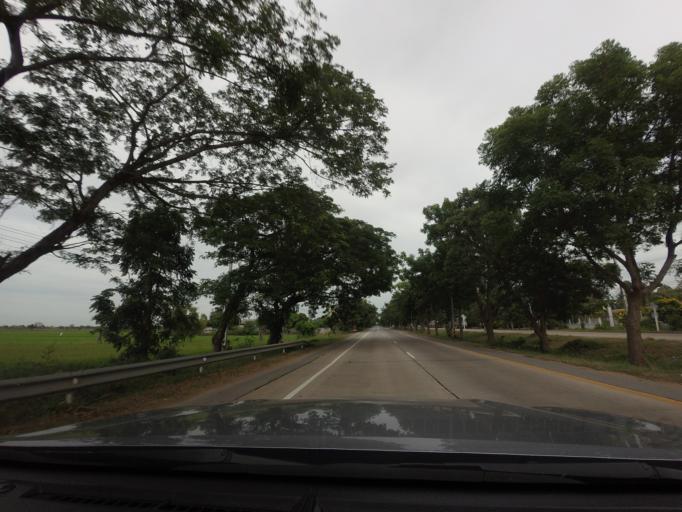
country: TH
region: Chai Nat
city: Sankhaburi
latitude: 15.0364
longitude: 100.1144
